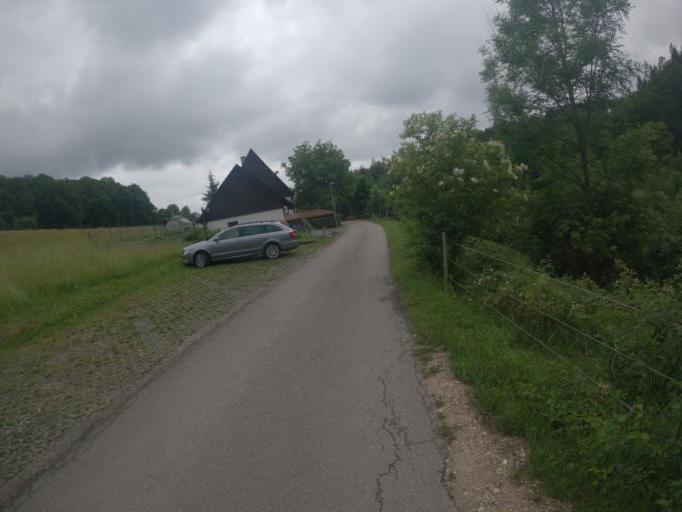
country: DE
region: Baden-Wuerttemberg
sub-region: Regierungsbezirk Stuttgart
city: Ebersbach an der Fils
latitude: 48.7457
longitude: 9.5409
